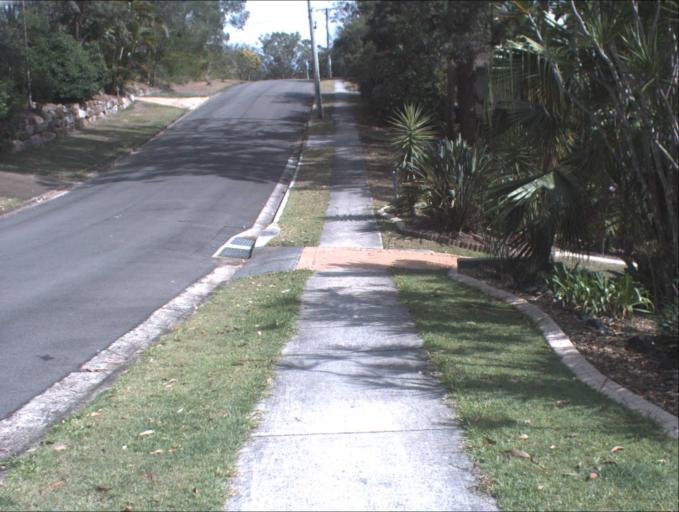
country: AU
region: Queensland
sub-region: Logan
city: Slacks Creek
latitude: -27.6264
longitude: 153.1519
